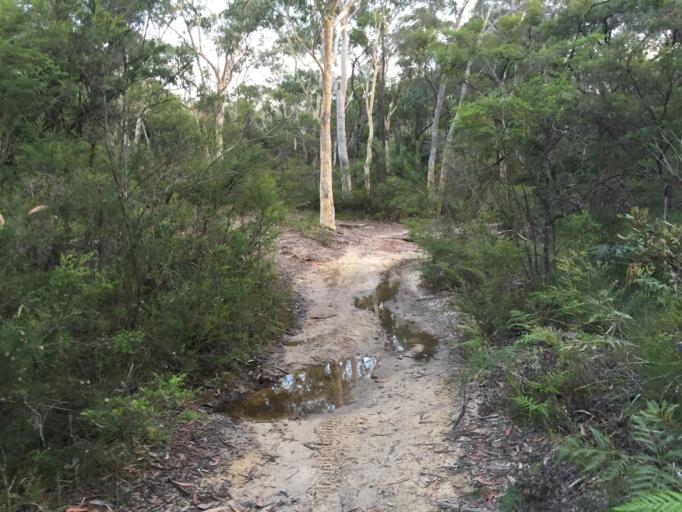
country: AU
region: New South Wales
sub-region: Blue Mountains Municipality
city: Blaxland
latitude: -33.7335
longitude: 150.6201
